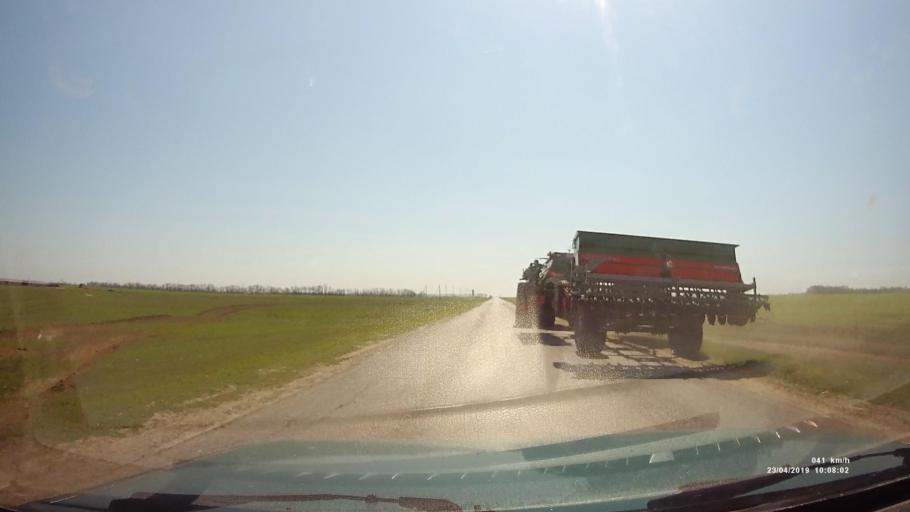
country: RU
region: Rostov
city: Sovetskoye
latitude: 46.7215
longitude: 42.2605
